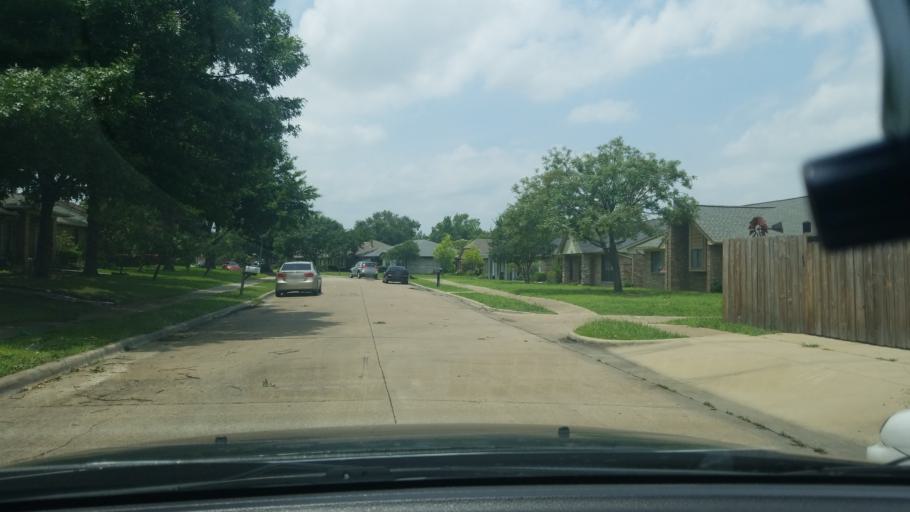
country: US
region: Texas
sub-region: Dallas County
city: Mesquite
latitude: 32.7993
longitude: -96.6124
